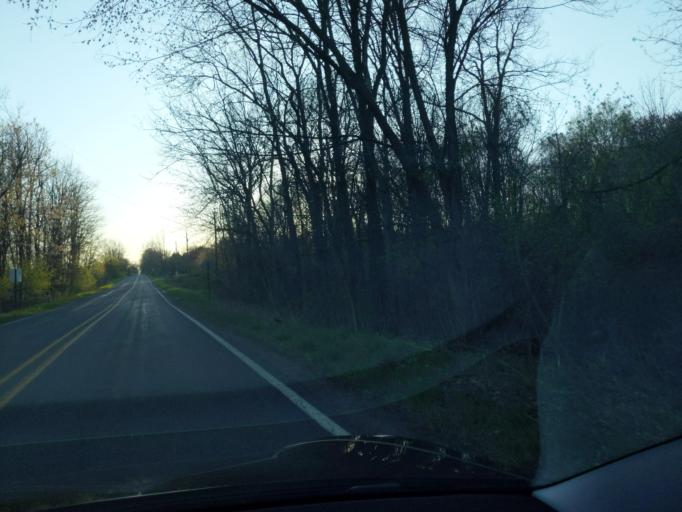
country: US
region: Michigan
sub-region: Ingham County
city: Stockbridge
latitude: 42.4831
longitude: -84.2234
